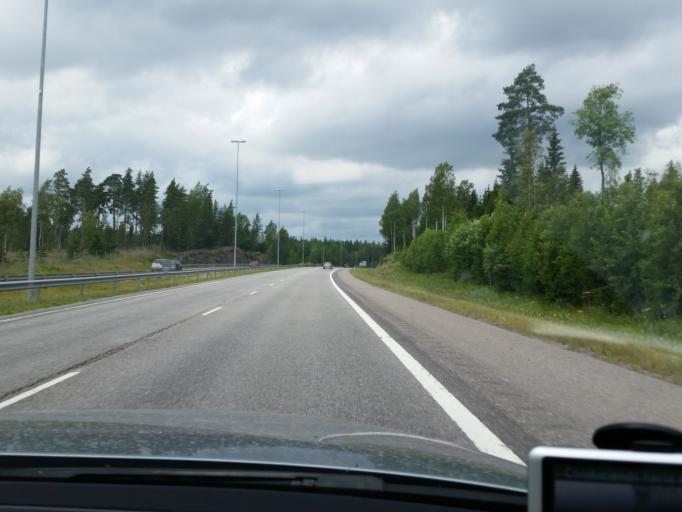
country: FI
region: Uusimaa
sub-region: Helsinki
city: Kirkkonummi
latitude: 60.2585
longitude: 24.4982
